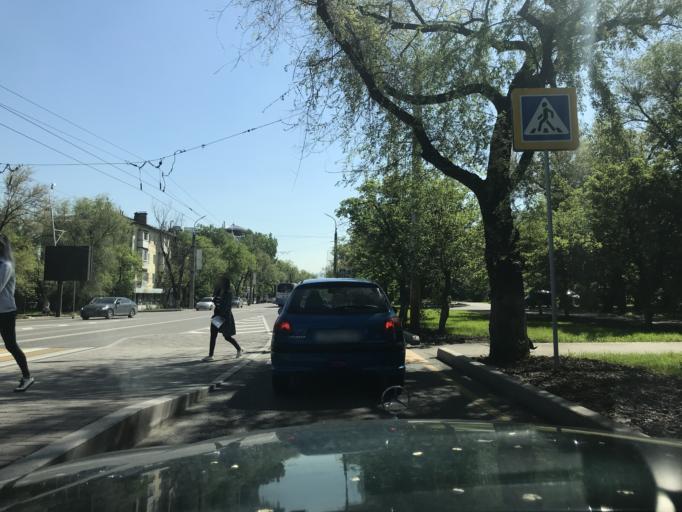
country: KZ
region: Almaty Qalasy
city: Almaty
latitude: 43.2252
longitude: 76.8977
